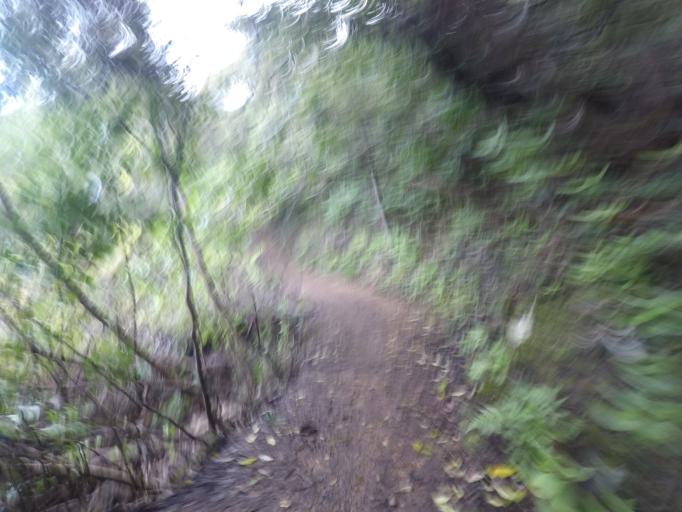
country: NZ
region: Bay of Plenty
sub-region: Western Bay of Plenty District
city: Waihi Beach
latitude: -37.3910
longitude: 175.9399
